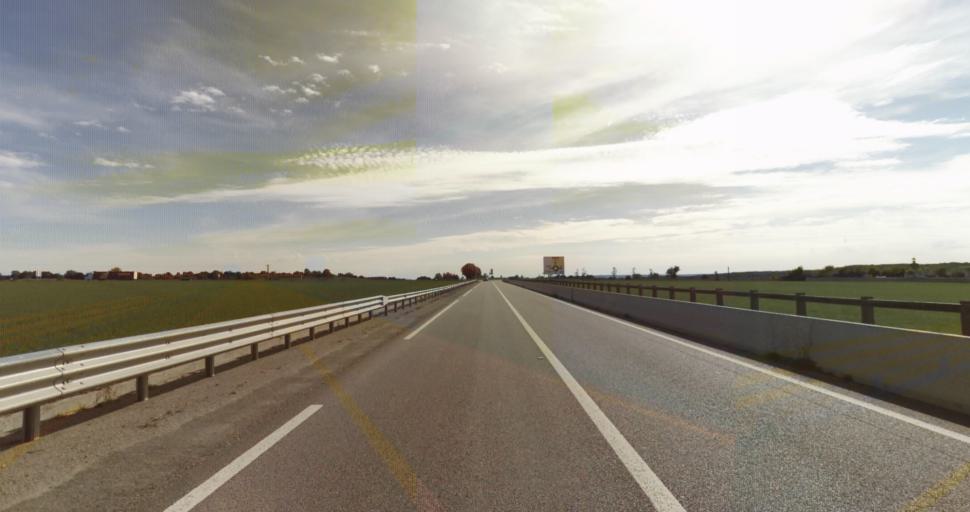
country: FR
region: Lower Normandy
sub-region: Departement de l'Orne
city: Sees
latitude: 48.7026
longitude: 0.2207
